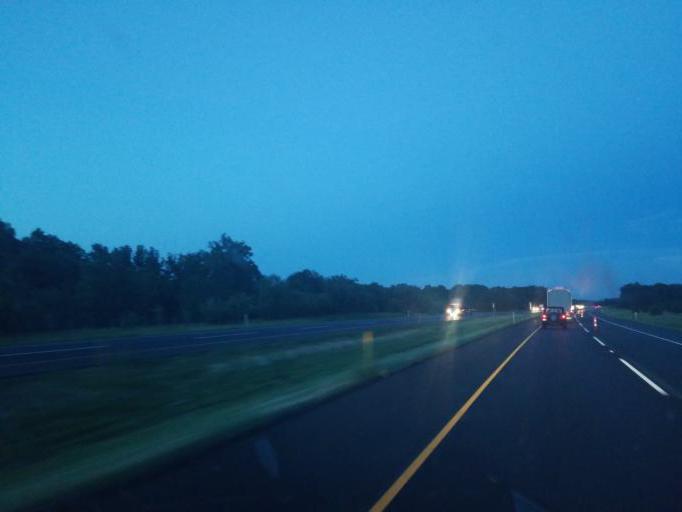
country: US
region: Indiana
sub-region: Saint Joseph County
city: Granger
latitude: 41.7335
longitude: -86.1072
